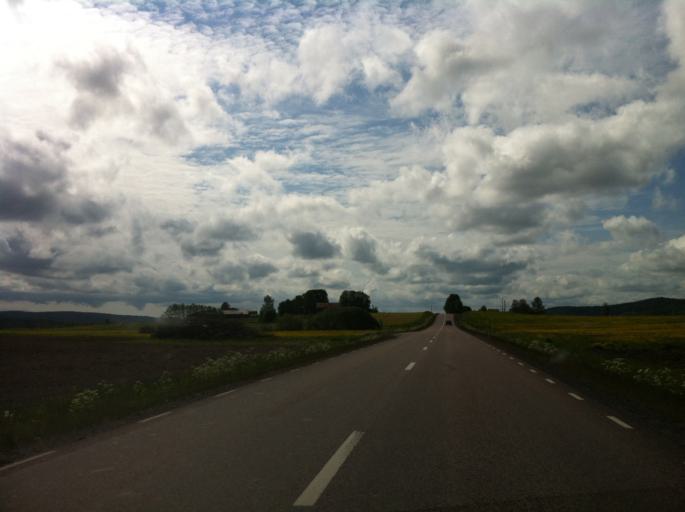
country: SE
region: Vaermland
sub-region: Sunne Kommun
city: Sunne
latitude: 59.6828
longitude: 13.1397
